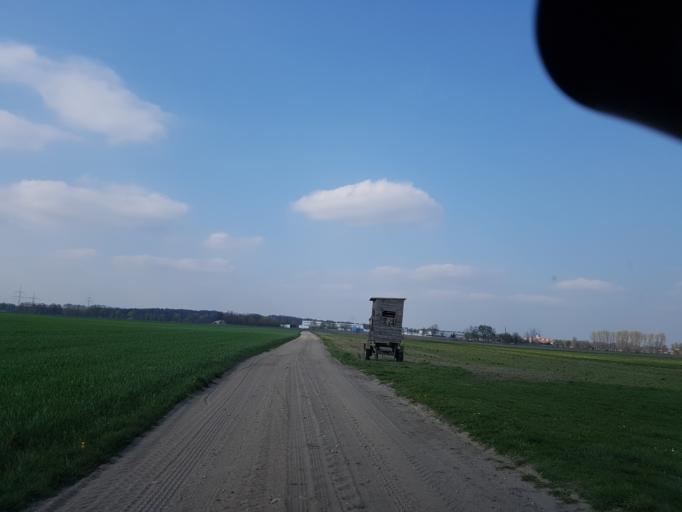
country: DE
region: Brandenburg
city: Ruckersdorf
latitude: 51.5978
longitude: 13.5328
